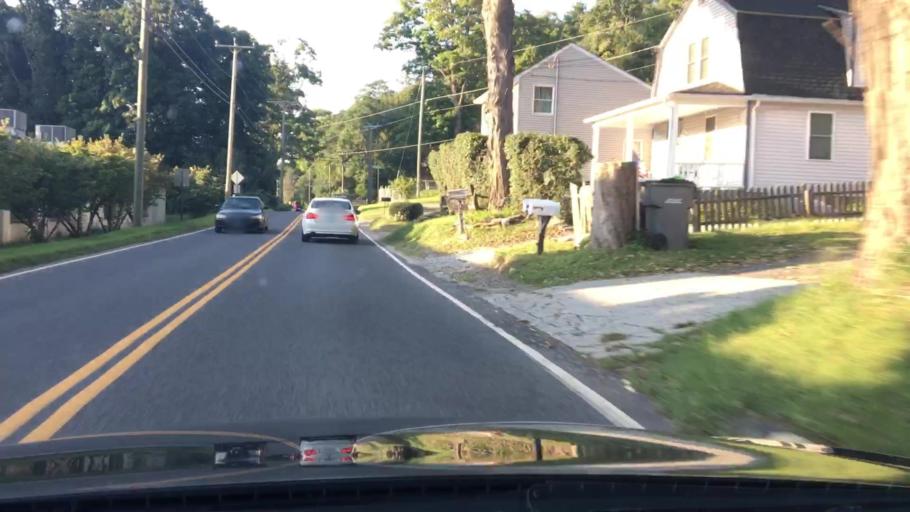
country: US
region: Connecticut
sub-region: Litchfield County
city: New Milford
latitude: 41.5674
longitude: -73.4056
